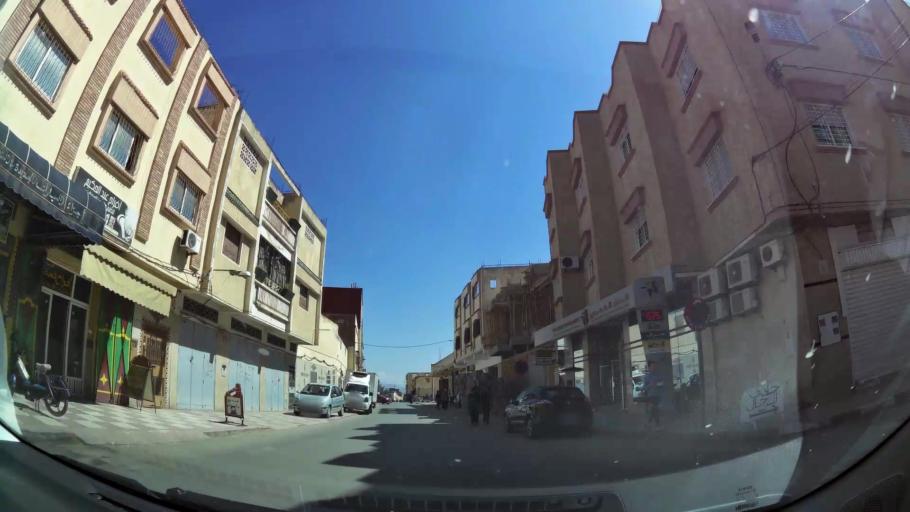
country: MA
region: Oriental
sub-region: Oujda-Angad
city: Oujda
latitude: 34.6853
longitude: -1.9322
